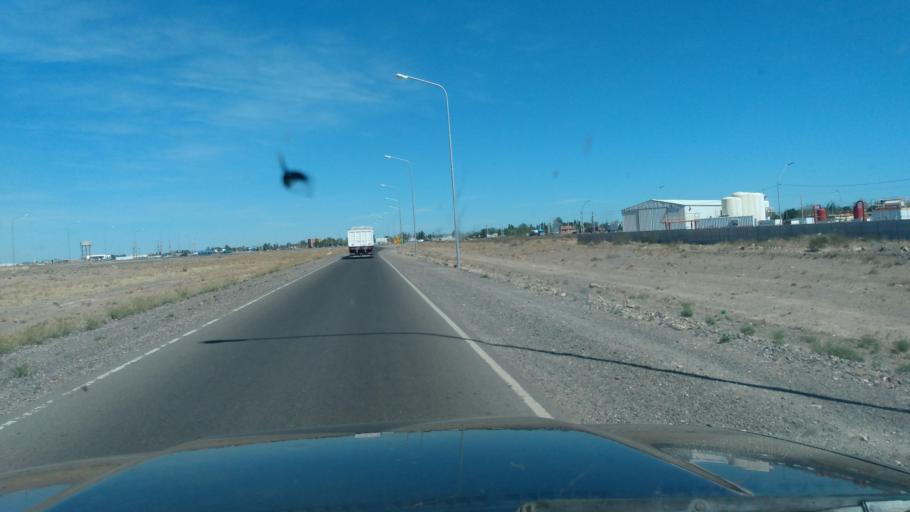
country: AR
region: Neuquen
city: Neuquen
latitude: -38.9131
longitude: -68.1158
